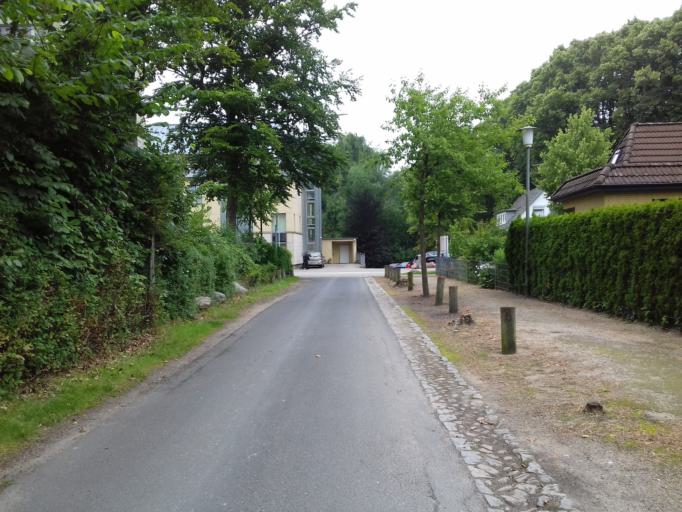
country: DE
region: Schleswig-Holstein
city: Neumunster
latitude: 54.0742
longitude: 9.9978
